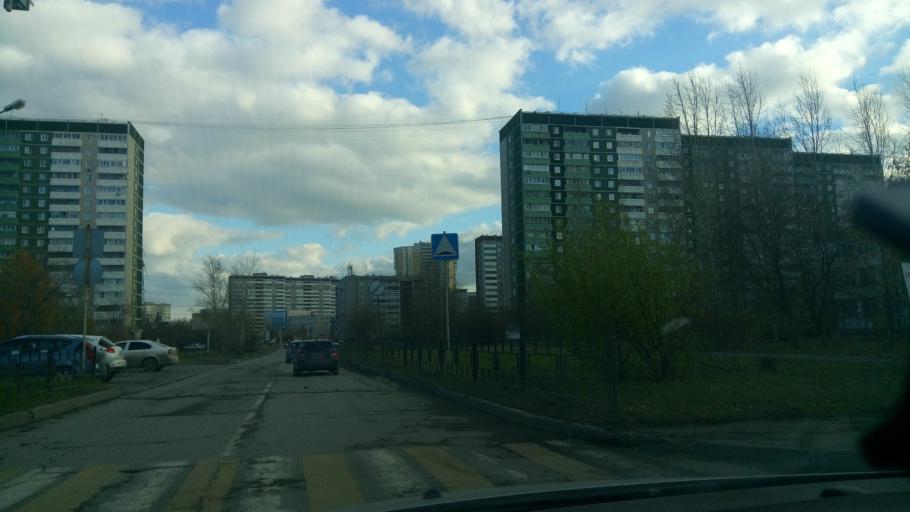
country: RU
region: Sverdlovsk
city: Yekaterinburg
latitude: 56.8665
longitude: 60.5395
